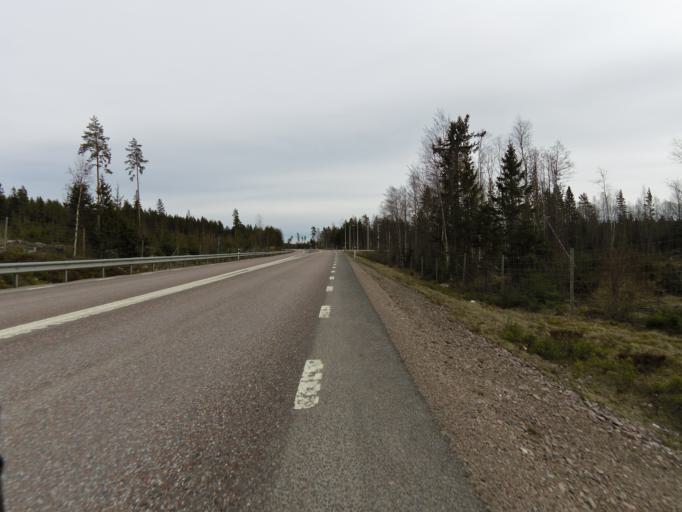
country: SE
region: Gaevleborg
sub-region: Hofors Kommun
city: Hofors
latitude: 60.5432
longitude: 16.2279
